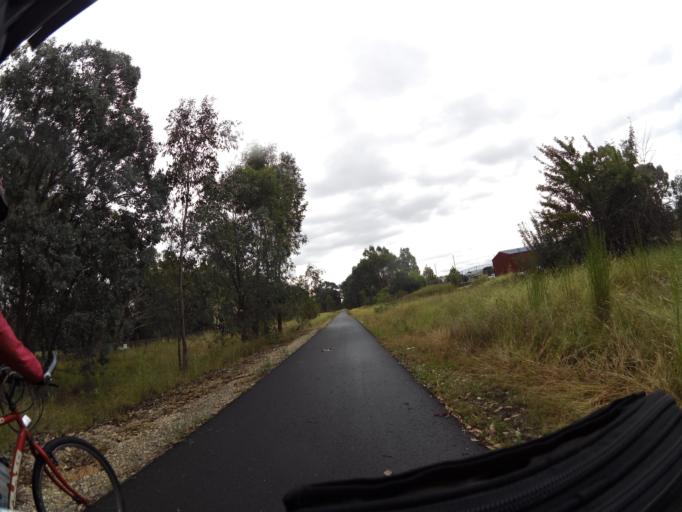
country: AU
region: Victoria
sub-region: Wodonga
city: Wodonga
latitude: -36.1406
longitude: 146.9112
